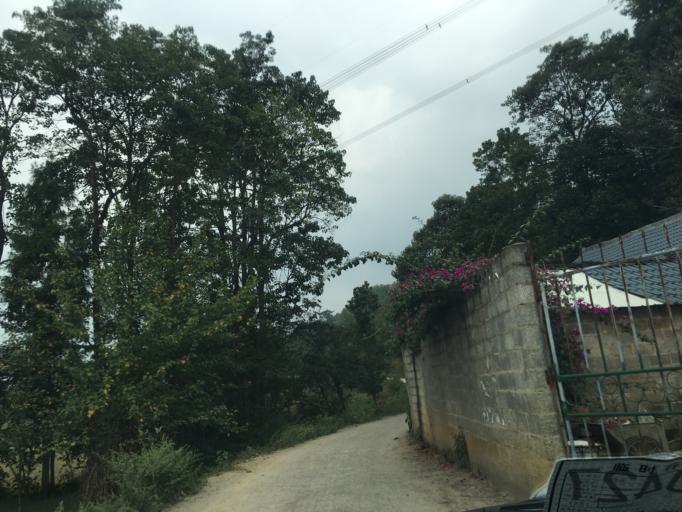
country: CN
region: Guangxi Zhuangzu Zizhiqu
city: Xinzhou
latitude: 25.5657
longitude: 105.6065
